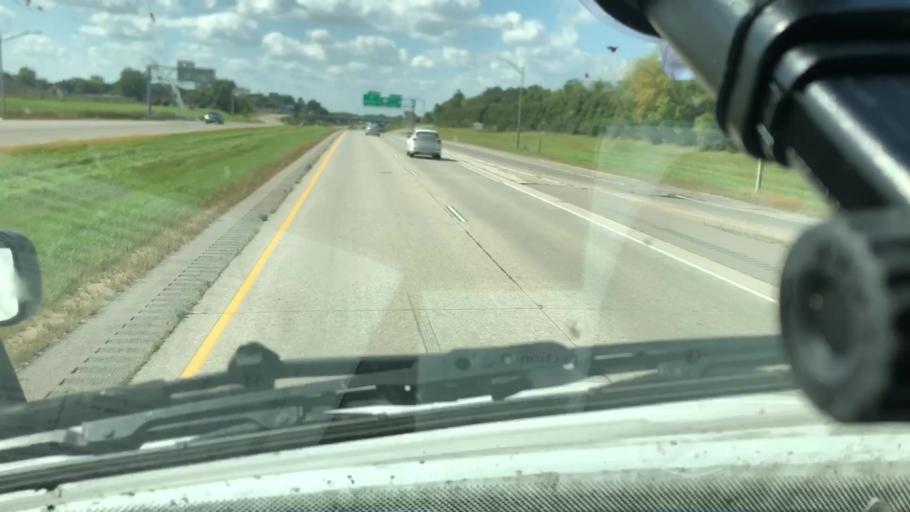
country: US
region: Minnesota
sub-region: Mower County
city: Austin
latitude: 43.6744
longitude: -92.9324
